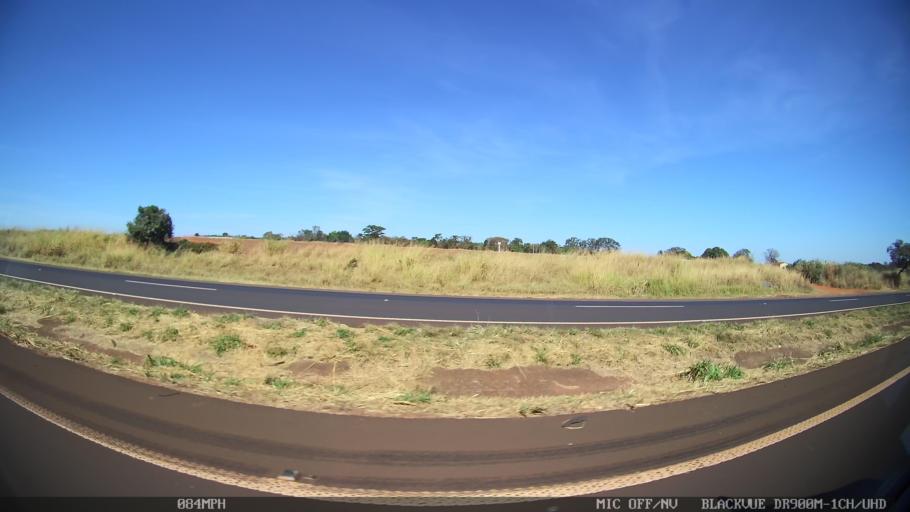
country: BR
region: Sao Paulo
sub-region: Barretos
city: Barretos
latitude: -20.5214
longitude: -48.5792
